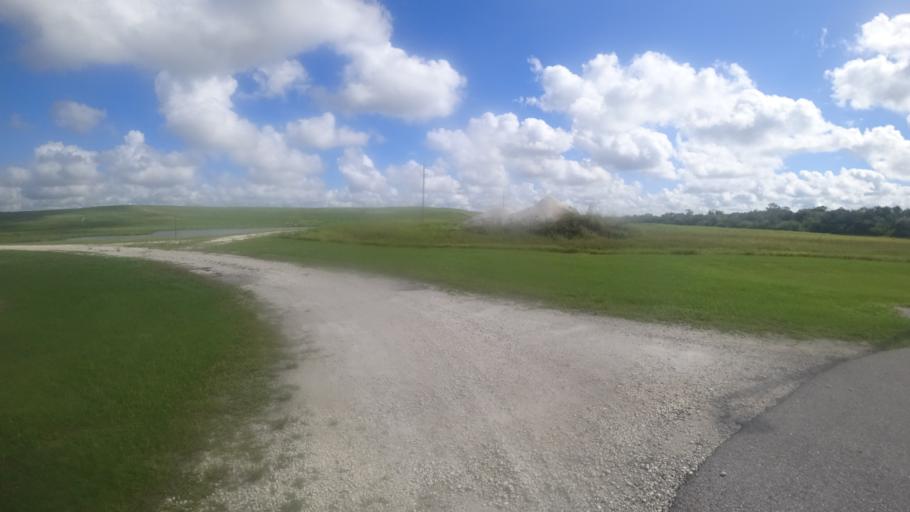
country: US
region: Florida
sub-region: Manatee County
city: Samoset
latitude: 27.4649
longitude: -82.4465
